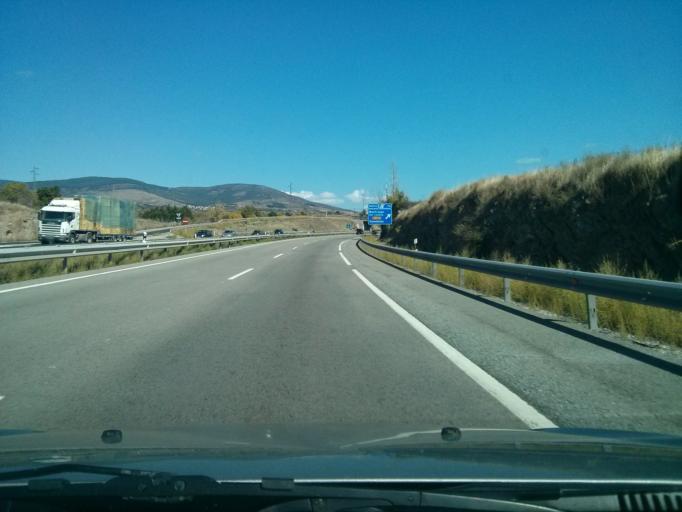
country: ES
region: Madrid
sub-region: Provincia de Madrid
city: Buitrago del Lozoya
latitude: 40.9957
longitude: -3.6417
